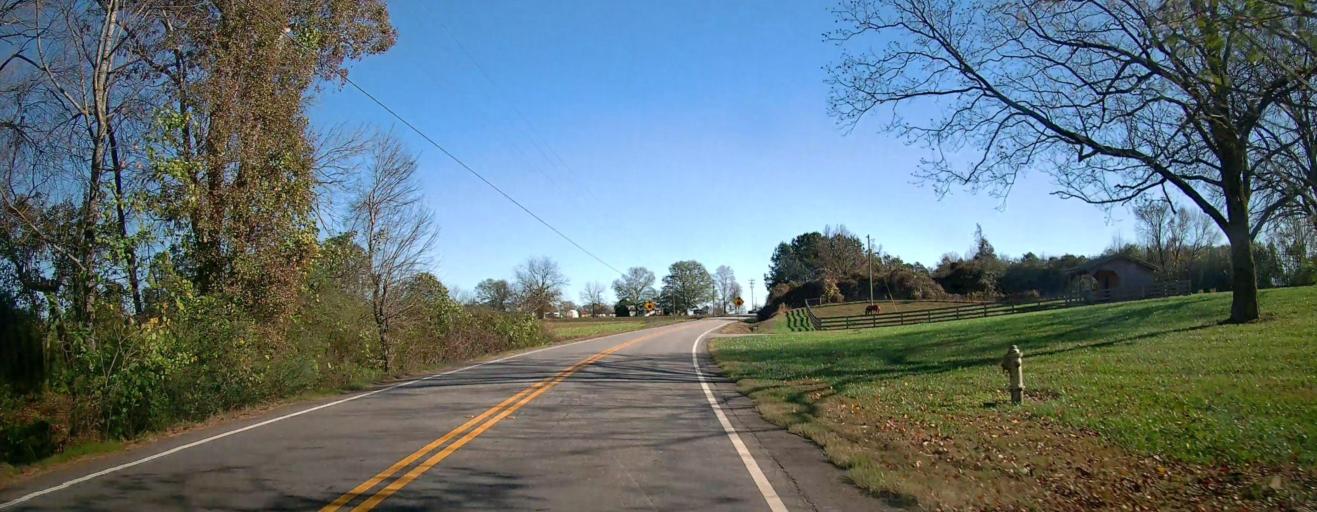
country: US
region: Georgia
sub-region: Hall County
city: Lula
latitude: 34.4722
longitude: -83.7360
